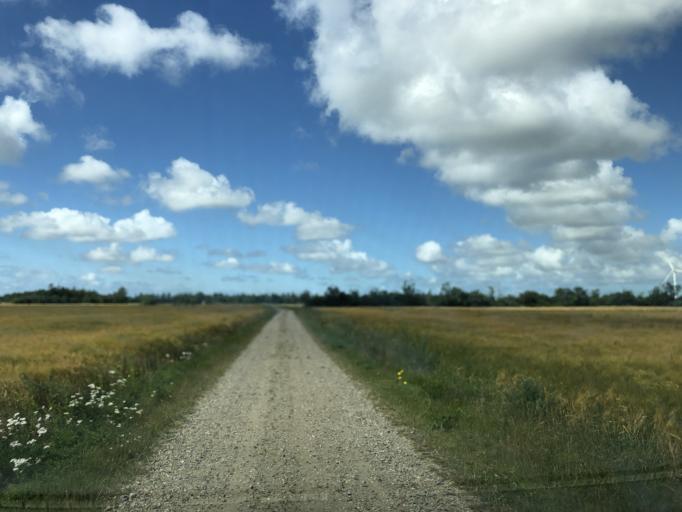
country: DK
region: Central Jutland
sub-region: Holstebro Kommune
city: Ulfborg
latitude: 56.3609
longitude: 8.3782
